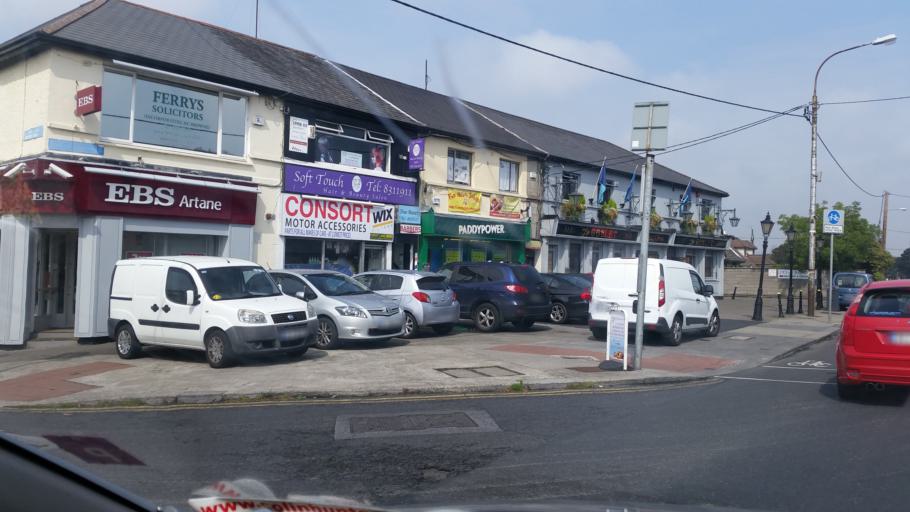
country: IE
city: Donnycarney
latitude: 53.3799
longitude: -6.2104
